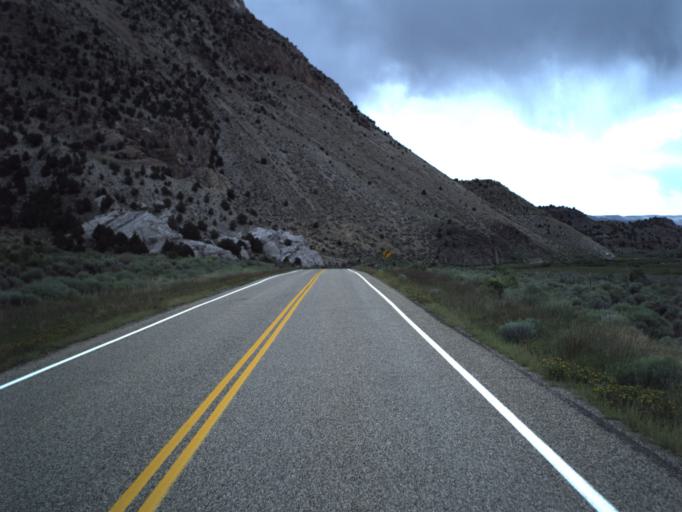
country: US
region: Utah
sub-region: Piute County
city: Junction
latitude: 38.1888
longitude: -112.0957
